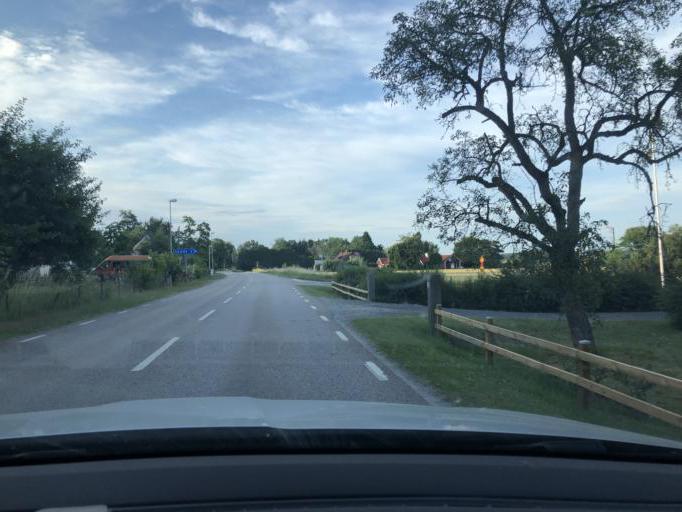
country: SE
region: Blekinge
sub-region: Solvesborgs Kommun
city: Soelvesborg
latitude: 56.1007
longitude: 14.6173
